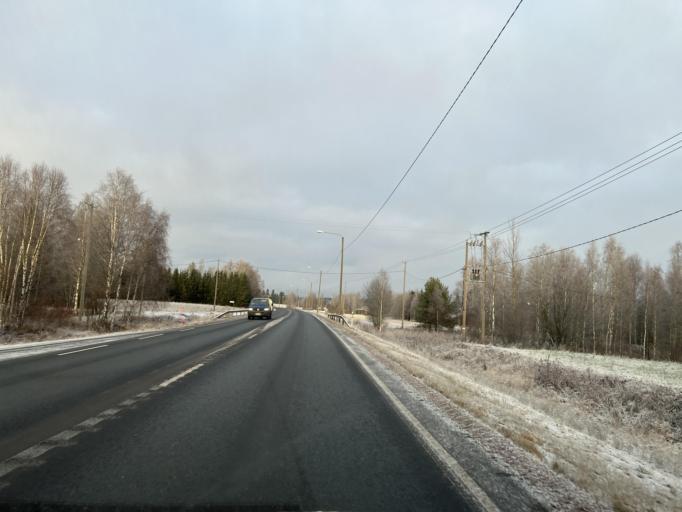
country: FI
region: Northern Ostrobothnia
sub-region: Oulu
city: Muhos
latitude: 64.8565
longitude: 25.8943
